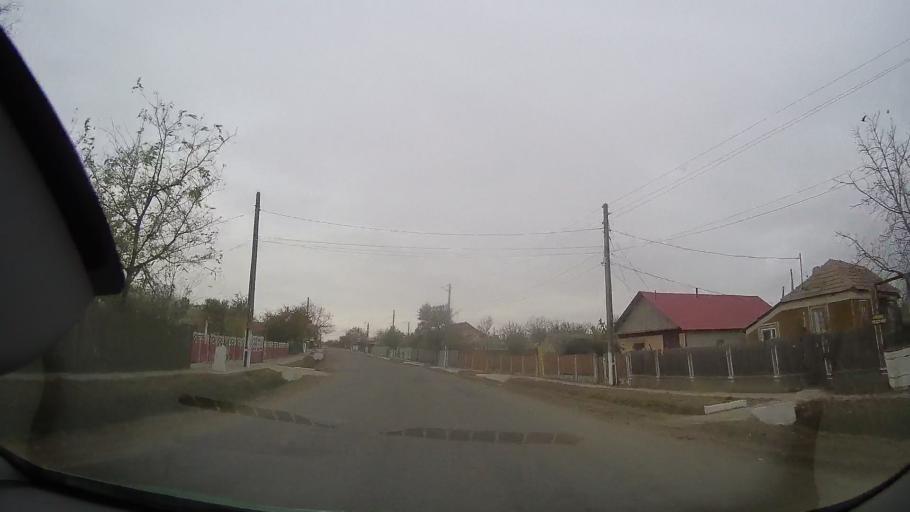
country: RO
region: Buzau
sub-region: Comuna Rusetu
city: Rusetu
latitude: 44.9540
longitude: 27.2174
